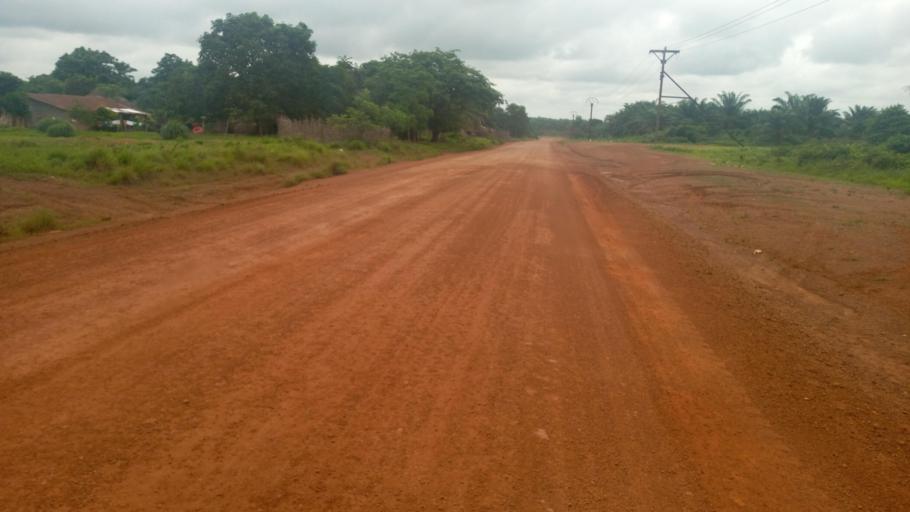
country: SL
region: Southern Province
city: Mogbwemo
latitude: 7.7240
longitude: -12.2820
